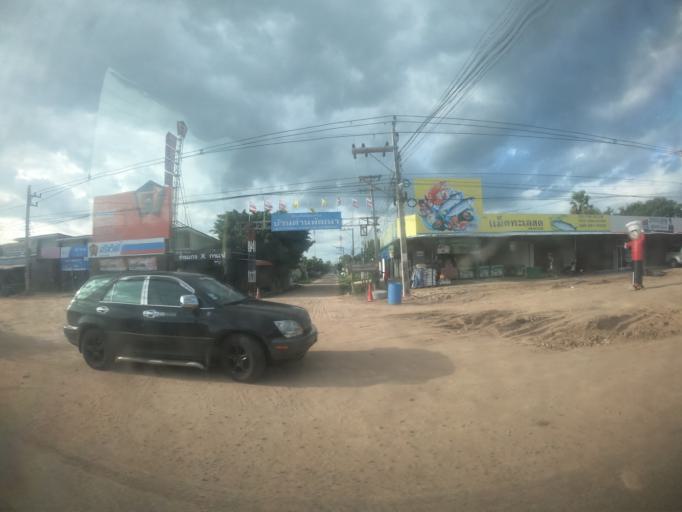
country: TH
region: Surin
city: Kap Choeng
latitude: 14.4551
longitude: 103.6828
